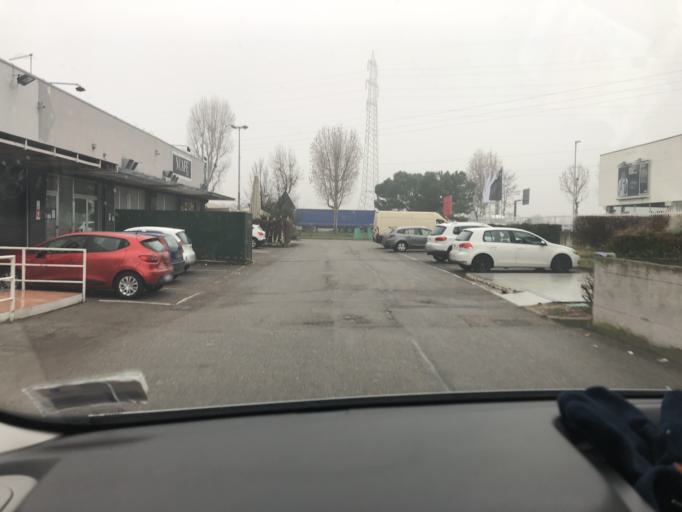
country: IT
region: Veneto
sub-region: Provincia di Verona
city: Lugagnano
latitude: 45.4473
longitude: 10.8756
